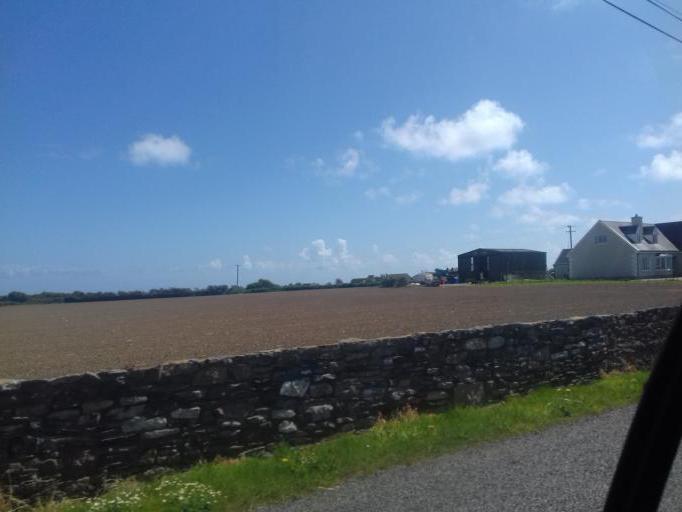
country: IE
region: Munster
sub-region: Waterford
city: Dunmore East
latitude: 52.1388
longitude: -6.9147
